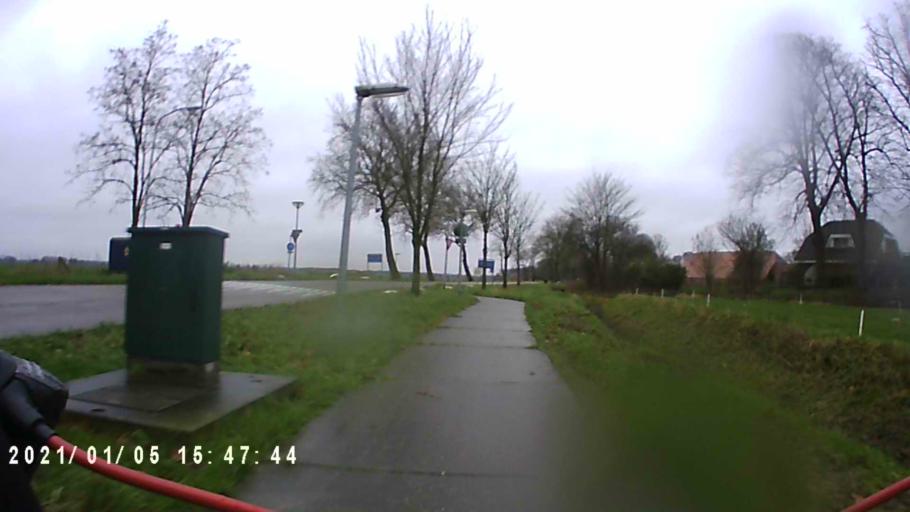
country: NL
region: Groningen
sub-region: Gemeente  Oldambt
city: Winschoten
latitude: 53.2019
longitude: 7.1146
